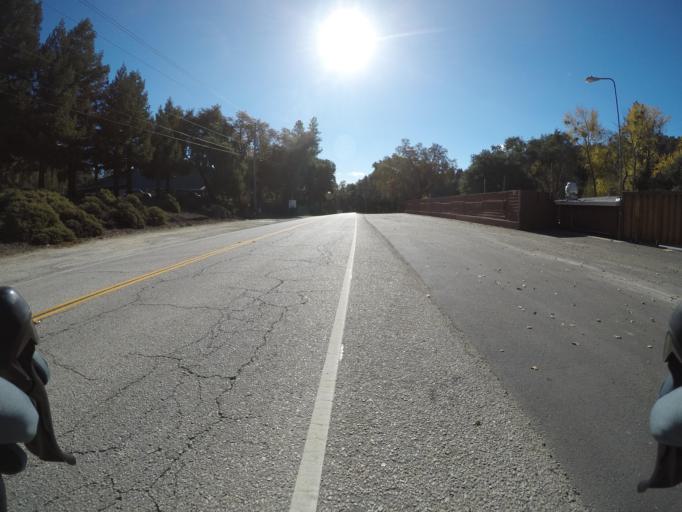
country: US
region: California
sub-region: Santa Cruz County
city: Mount Hermon
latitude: 37.0676
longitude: -122.0573
